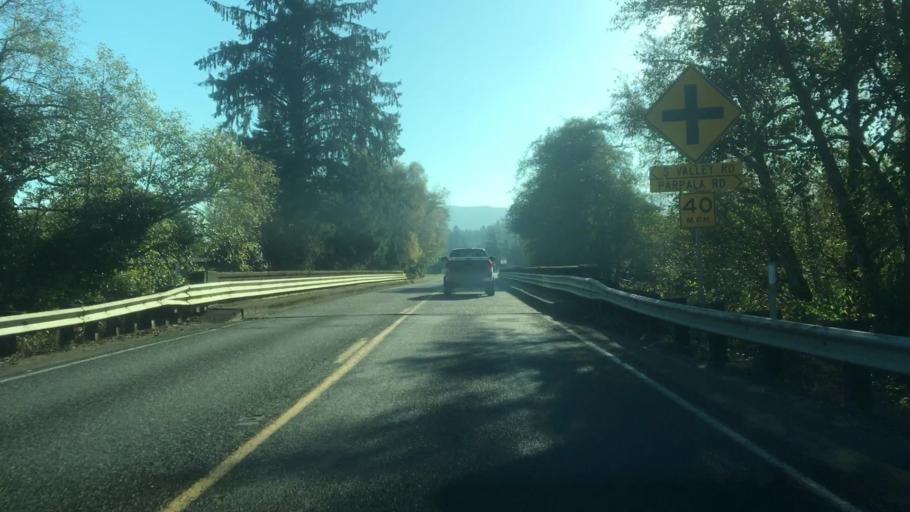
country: US
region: Oregon
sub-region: Clatsop County
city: Astoria
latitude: 46.3679
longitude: -123.8088
